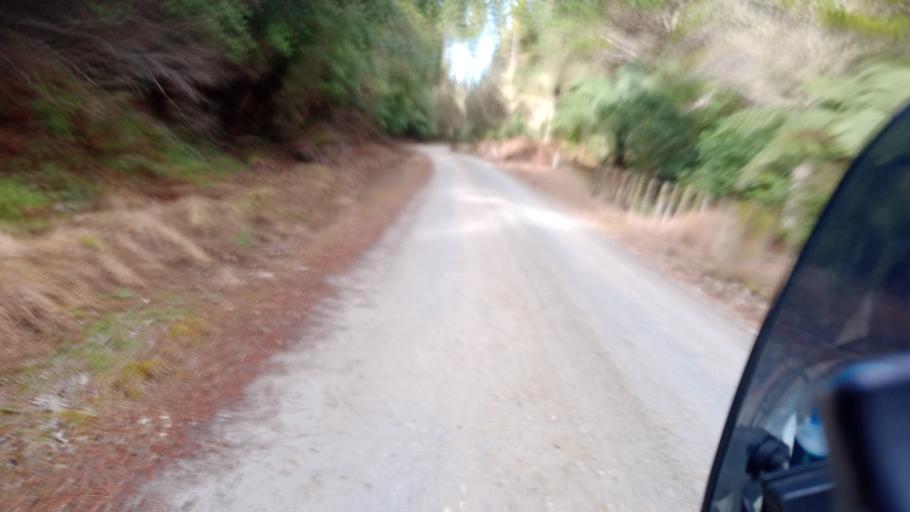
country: NZ
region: Gisborne
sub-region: Gisborne District
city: Gisborne
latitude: -38.8563
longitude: 177.7959
